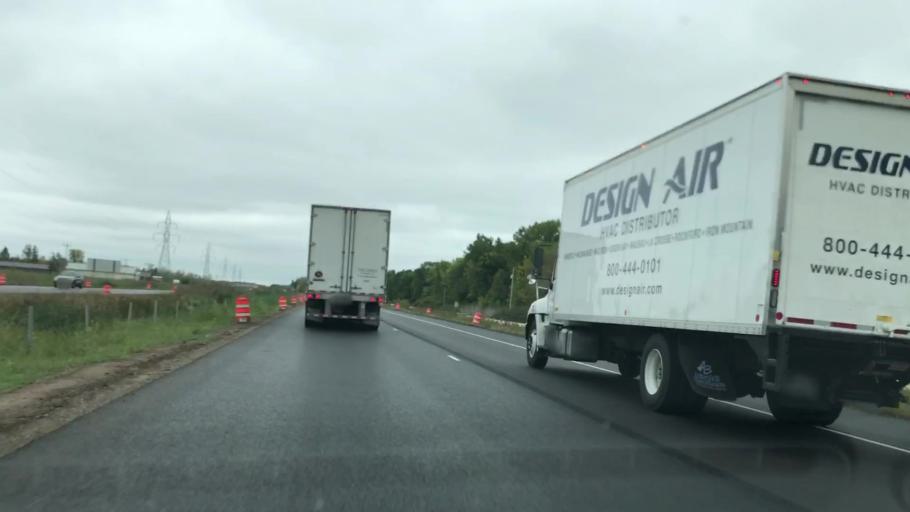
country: US
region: Wisconsin
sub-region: Brown County
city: Suamico
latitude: 44.6073
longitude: -88.0503
